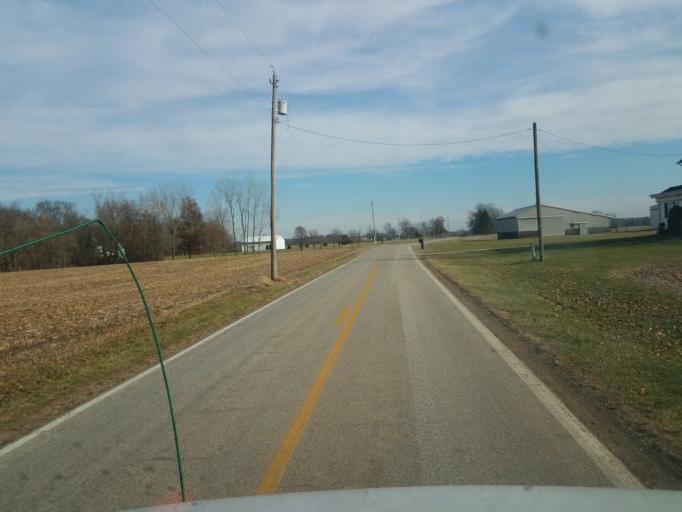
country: US
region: Ohio
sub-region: Delaware County
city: Ashley
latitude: 40.3570
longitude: -82.9826
